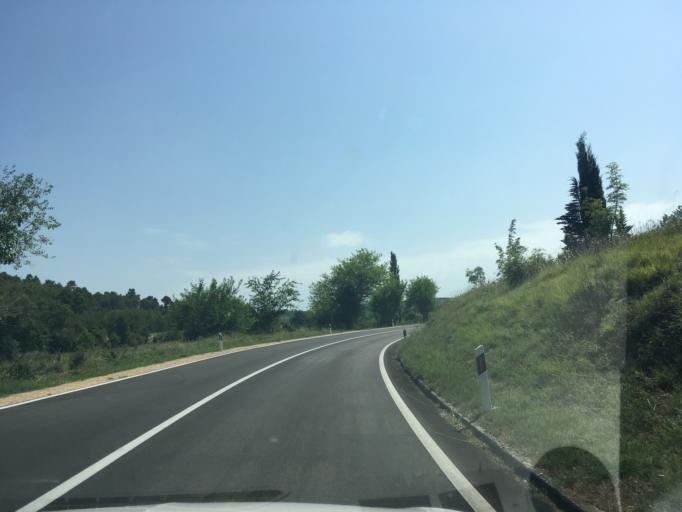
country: HR
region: Sibensko-Kniniska
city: Zaton
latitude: 43.9260
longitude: 15.8125
